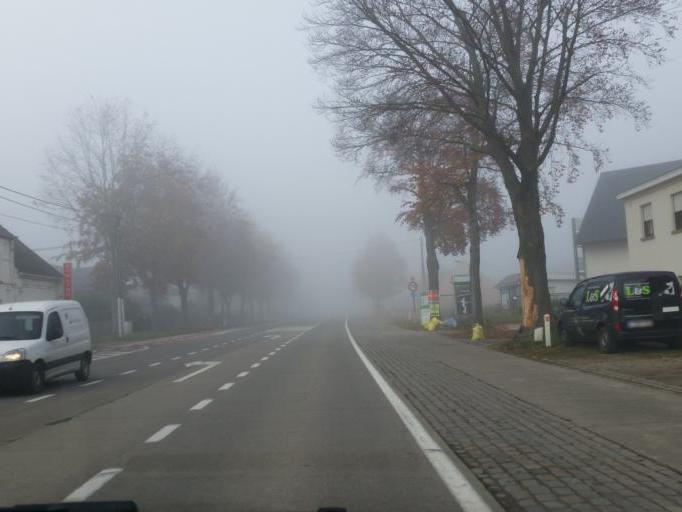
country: BE
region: Flanders
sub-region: Provincie Oost-Vlaanderen
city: Lede
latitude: 50.9472
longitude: 3.9518
